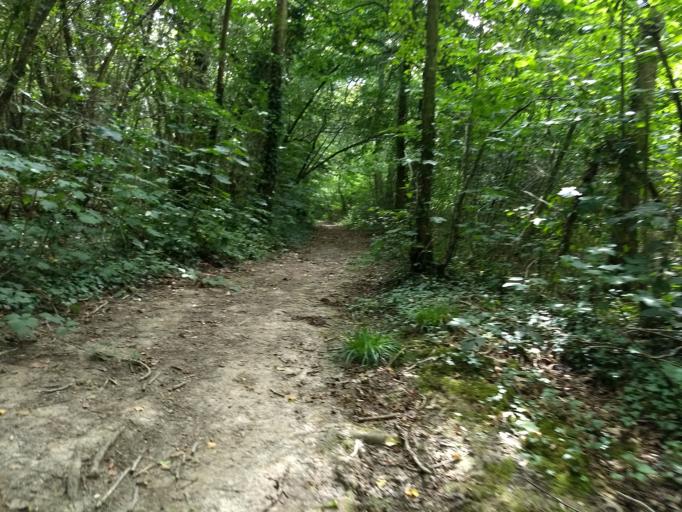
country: GB
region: England
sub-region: Isle of Wight
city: Newport
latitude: 50.7180
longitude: -1.2594
